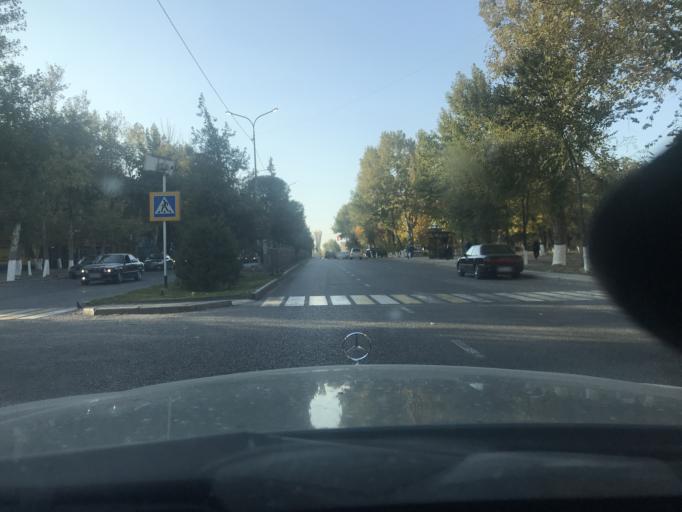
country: KZ
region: Ongtustik Qazaqstan
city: Shymkent
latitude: 42.3031
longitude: 69.6041
